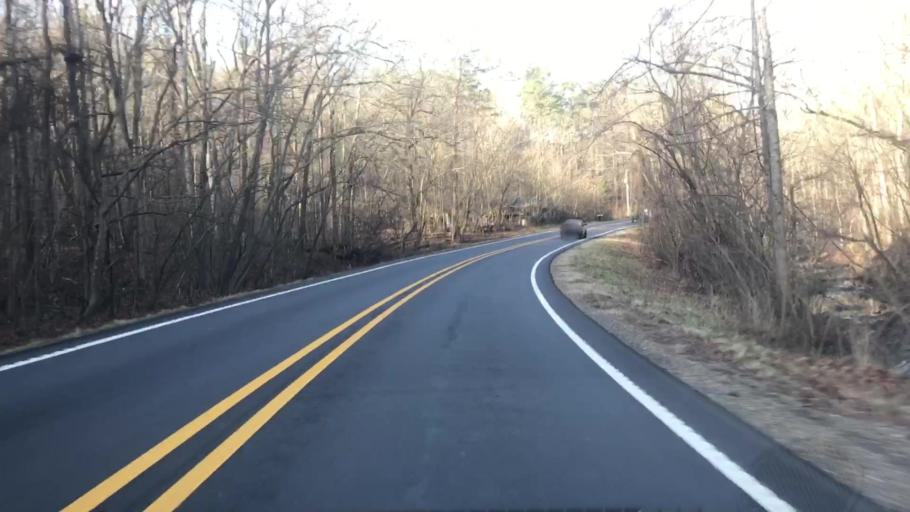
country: US
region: Arkansas
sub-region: Montgomery County
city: Mount Ida
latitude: 34.5228
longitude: -93.3976
